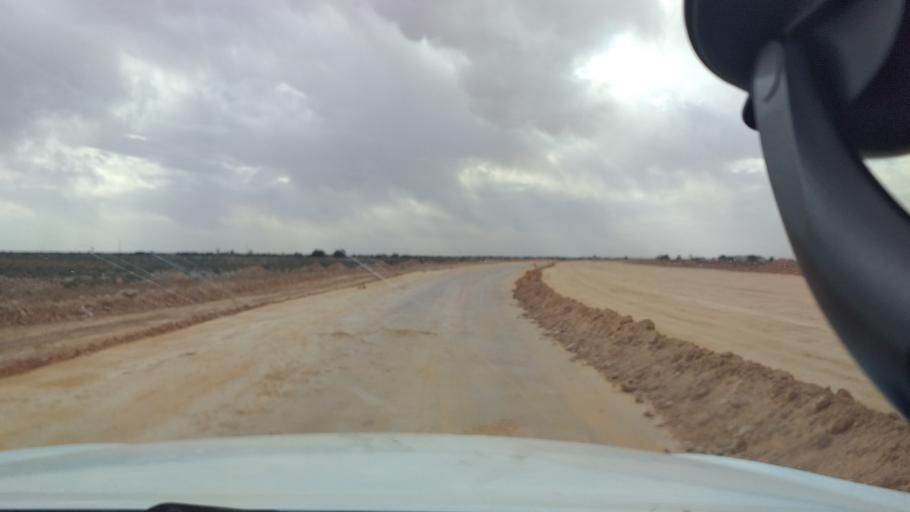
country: TN
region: Madanin
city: Medenine
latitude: 33.3089
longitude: 10.6136
